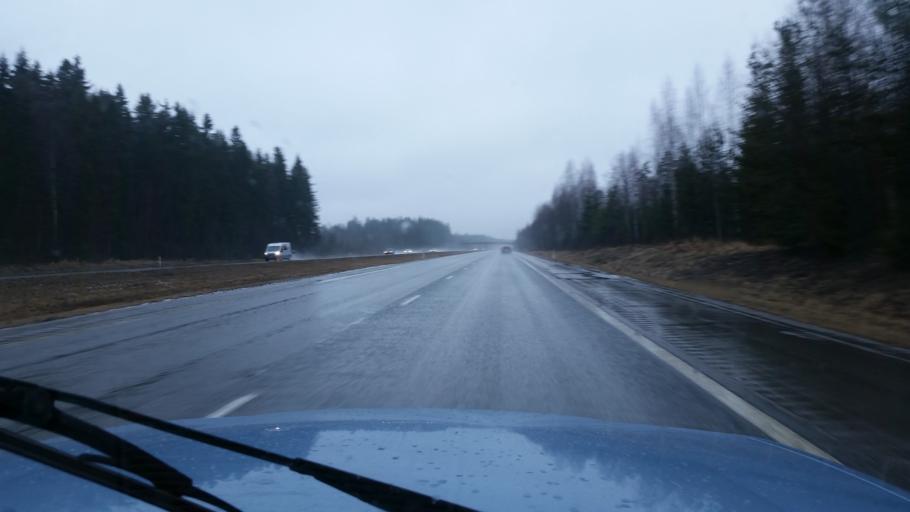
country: FI
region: Haeme
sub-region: Haemeenlinna
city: Tervakoski
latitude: 60.7898
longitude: 24.6976
